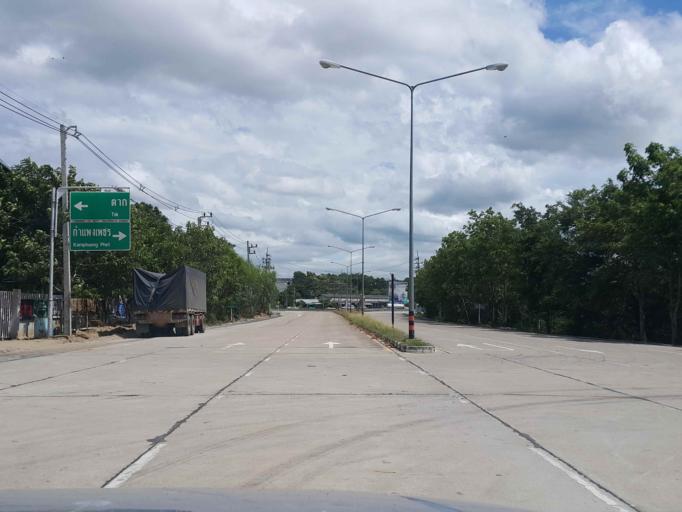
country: TH
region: Tak
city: Tak
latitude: 16.8555
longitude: 99.1169
